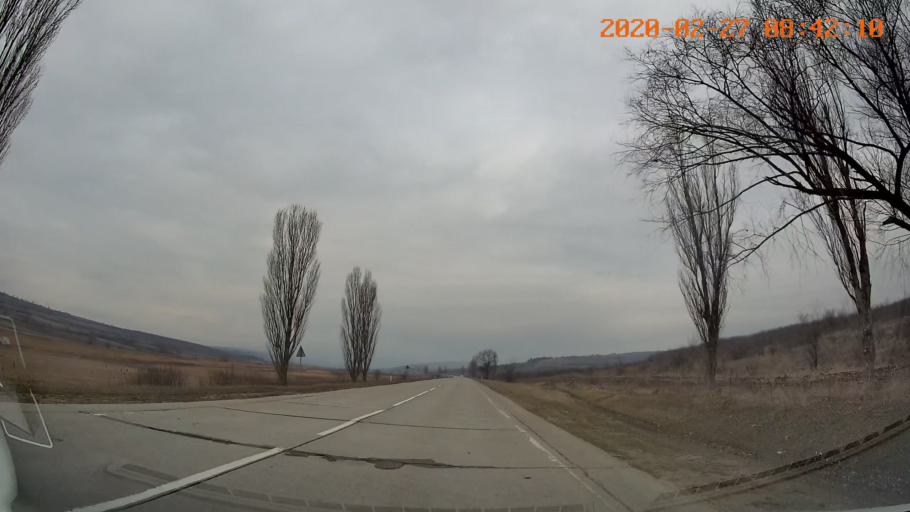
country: MD
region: Taraclia
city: Telenesti
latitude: 47.3963
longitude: 28.3331
